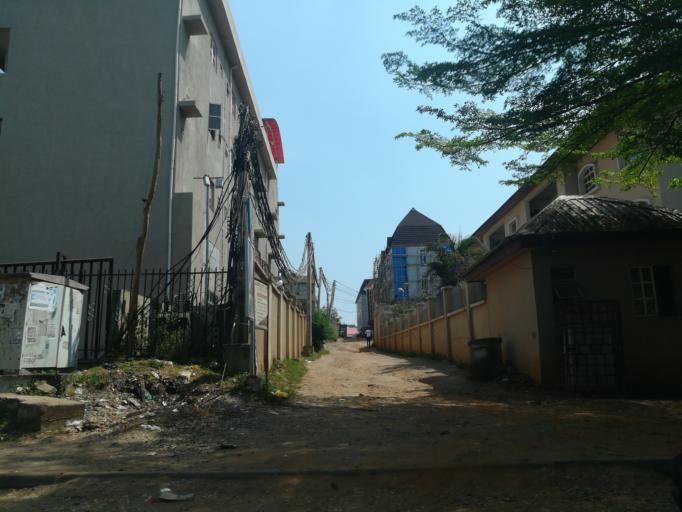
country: NG
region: Abuja Federal Capital Territory
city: Abuja
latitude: 9.0716
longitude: 7.4372
